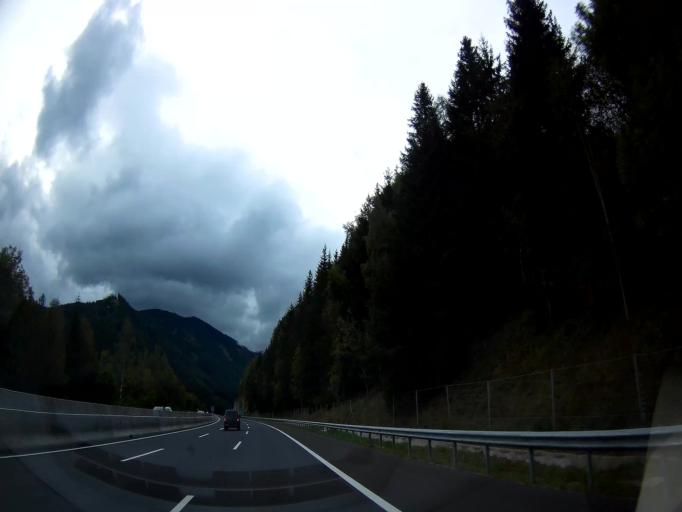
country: AT
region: Styria
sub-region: Politischer Bezirk Graz-Umgebung
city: Ubelbach
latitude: 47.2465
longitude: 15.1776
